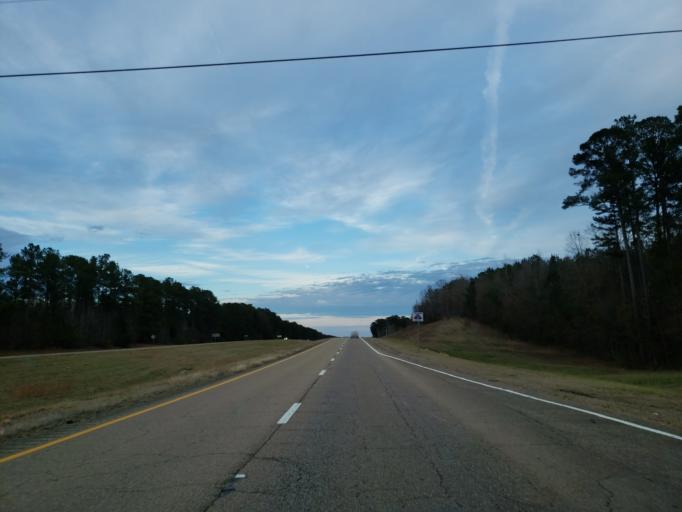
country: US
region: Mississippi
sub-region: Lauderdale County
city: Meridian Station
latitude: 32.4924
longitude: -88.5810
